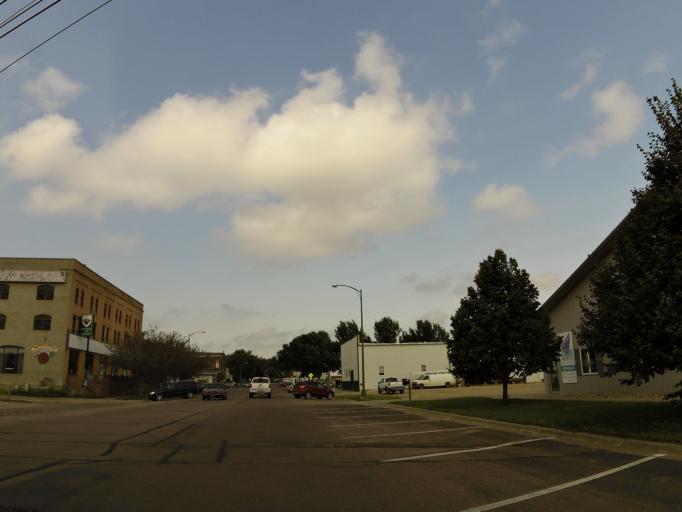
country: US
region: South Dakota
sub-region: Codington County
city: Watertown
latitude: 44.9022
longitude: -97.1139
